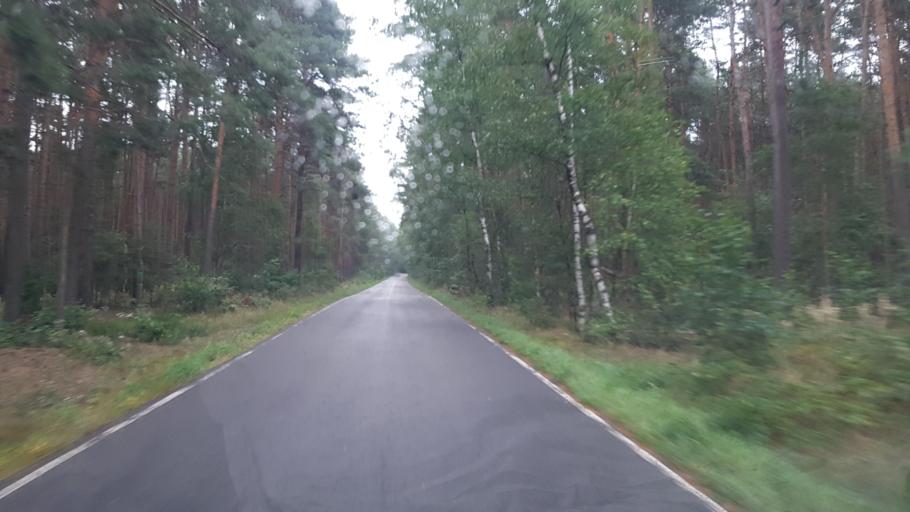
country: DE
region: Brandenburg
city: Lindenau
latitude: 51.4011
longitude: 13.7508
